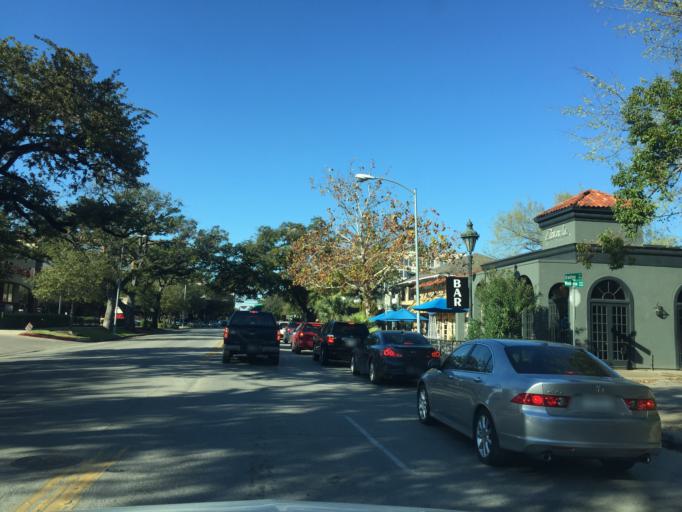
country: US
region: Texas
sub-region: Harris County
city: Houston
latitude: 29.7332
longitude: -95.3912
